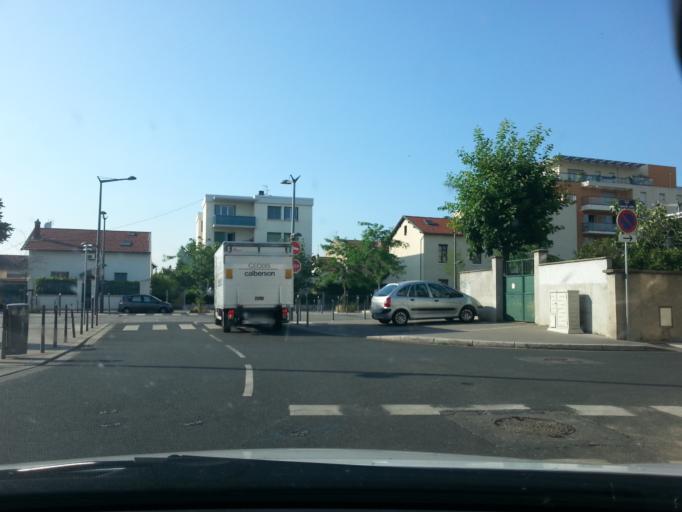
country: FR
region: Rhone-Alpes
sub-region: Departement du Rhone
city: Lyon
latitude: 45.7301
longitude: 4.8568
